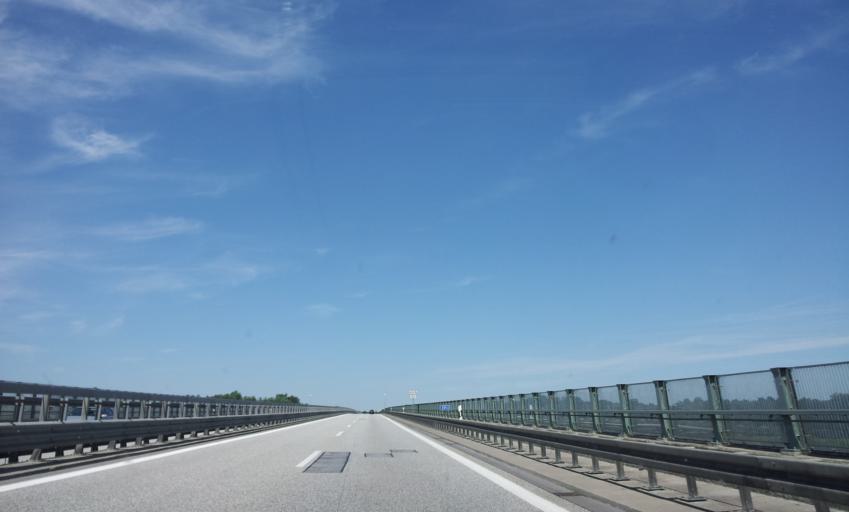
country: DE
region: Mecklenburg-Vorpommern
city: Jarmen
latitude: 53.9221
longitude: 13.3510
